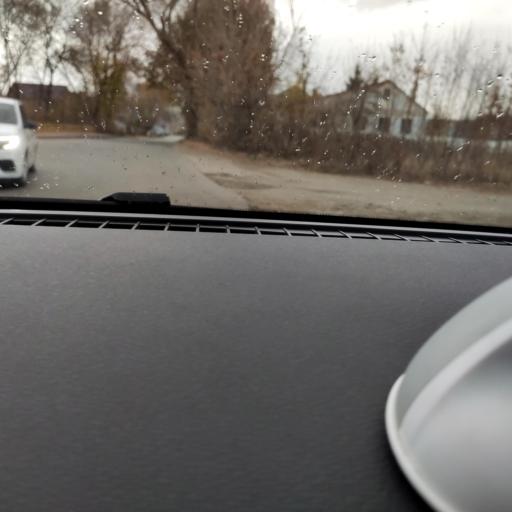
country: RU
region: Samara
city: Petra-Dubrava
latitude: 53.2951
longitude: 50.3045
